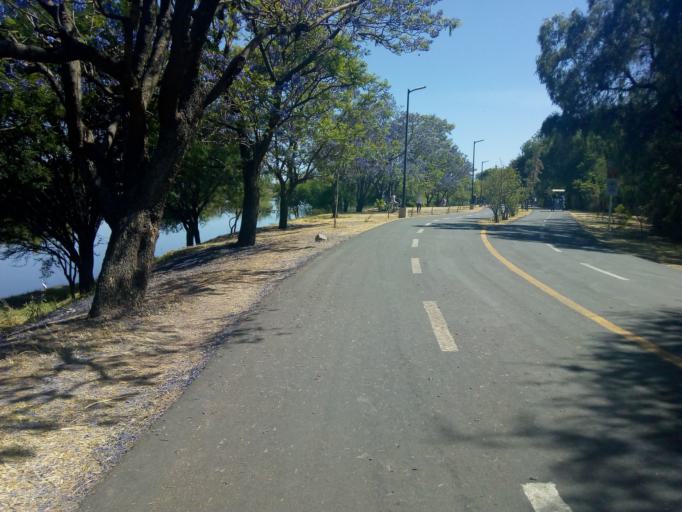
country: MX
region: Guanajuato
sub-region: Leon
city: La Ermita
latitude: 21.1798
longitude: -101.6963
